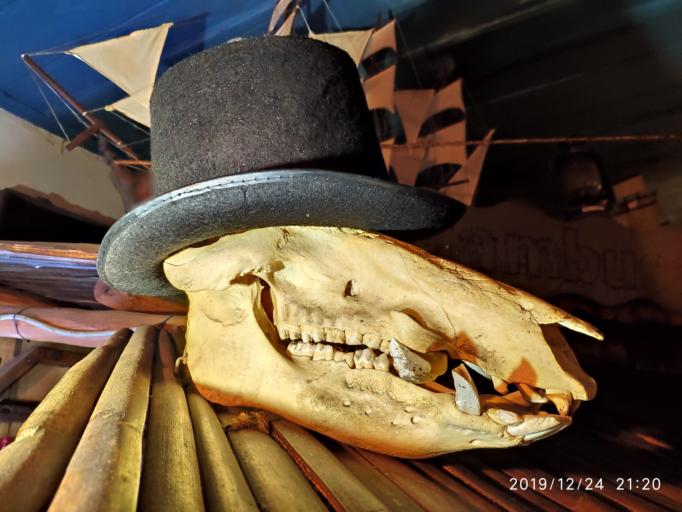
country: MG
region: Diana
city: Antsiranana
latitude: -12.2763
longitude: 49.2925
